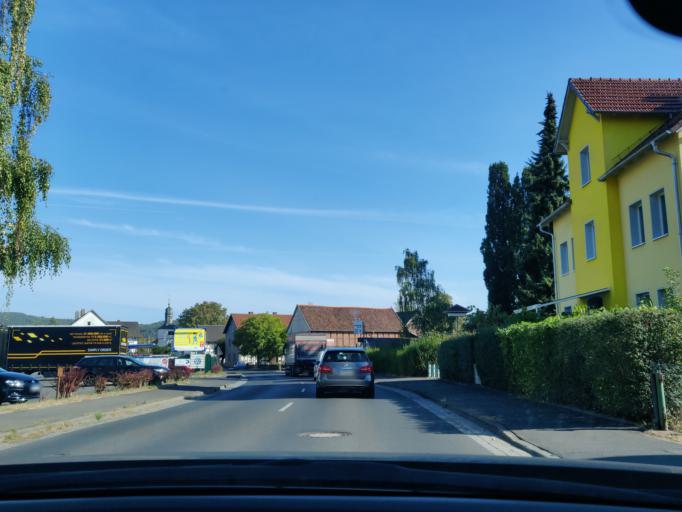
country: DE
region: Hesse
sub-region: Regierungsbezirk Kassel
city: Bad Wildungen
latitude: 51.1298
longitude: 9.1756
